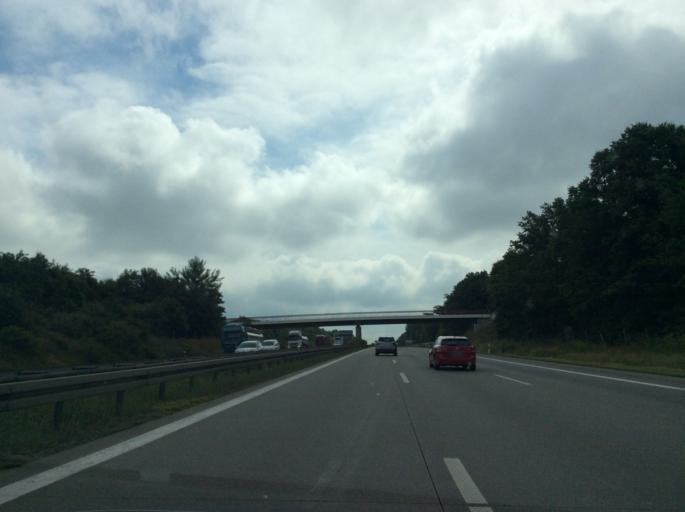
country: DE
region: Brandenburg
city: Wildau
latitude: 52.3110
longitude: 13.6135
